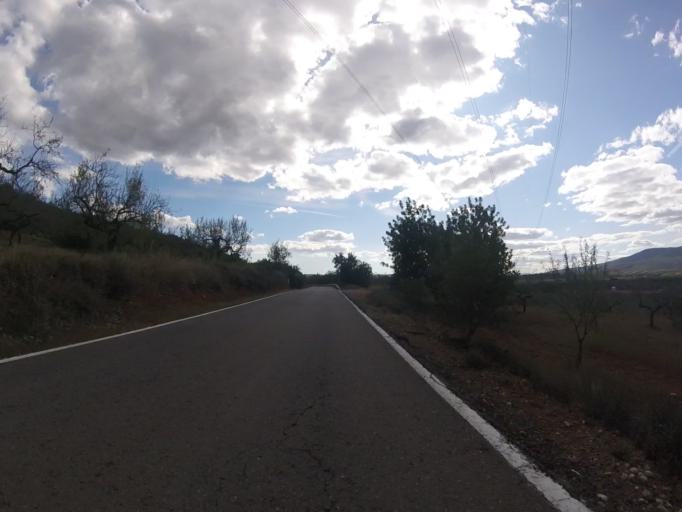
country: ES
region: Valencia
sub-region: Provincia de Castello
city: Cuevas de Vinroma
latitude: 40.3579
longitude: 0.1256
